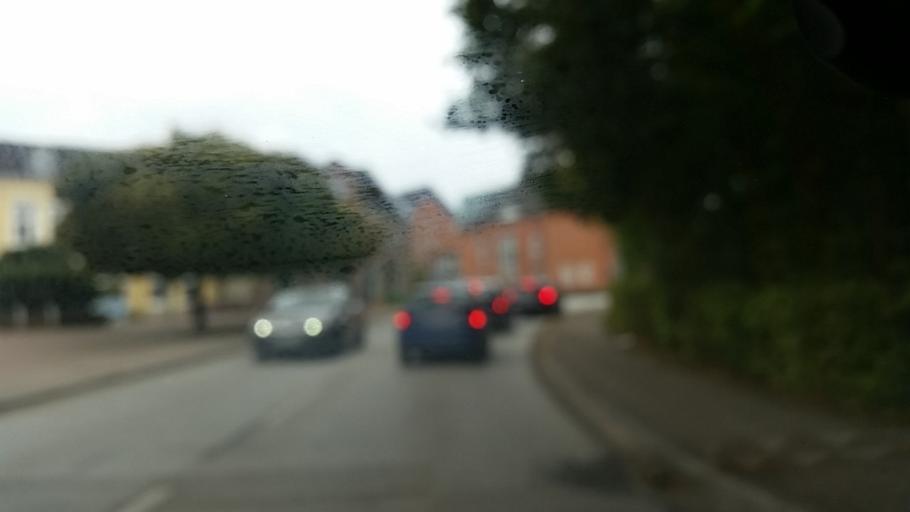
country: DE
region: Schleswig-Holstein
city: Bad Segeberg
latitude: 53.9371
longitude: 10.3050
